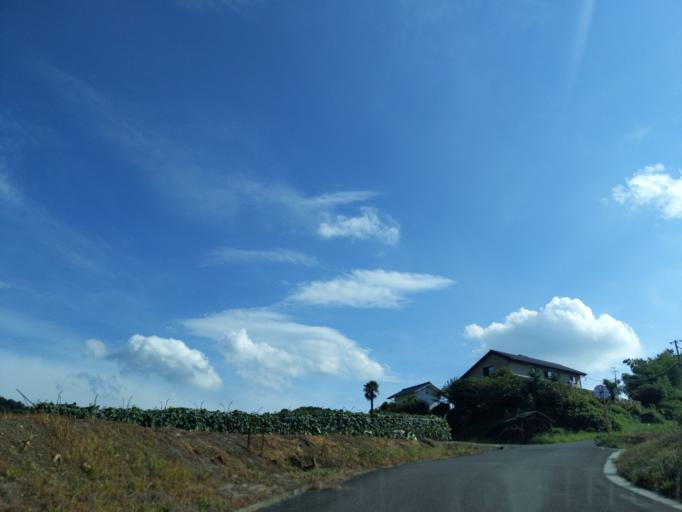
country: JP
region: Fukushima
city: Koriyama
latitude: 37.4023
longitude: 140.4299
